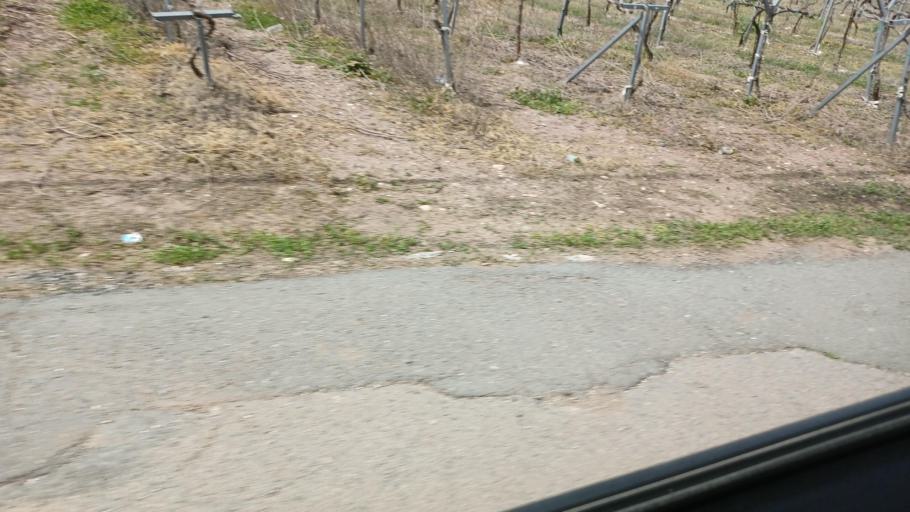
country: CY
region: Pafos
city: Pegeia
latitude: 34.9563
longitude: 32.4021
